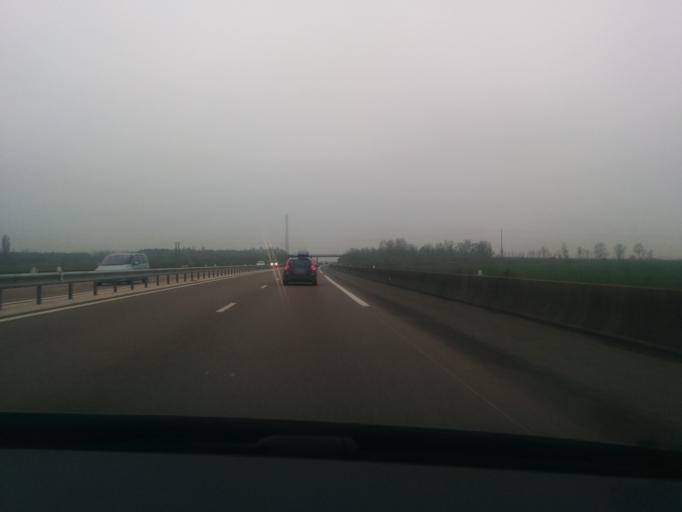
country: FR
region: Bourgogne
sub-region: Departement de la Cote-d'Or
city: Genlis
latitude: 47.2476
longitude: 5.2404
